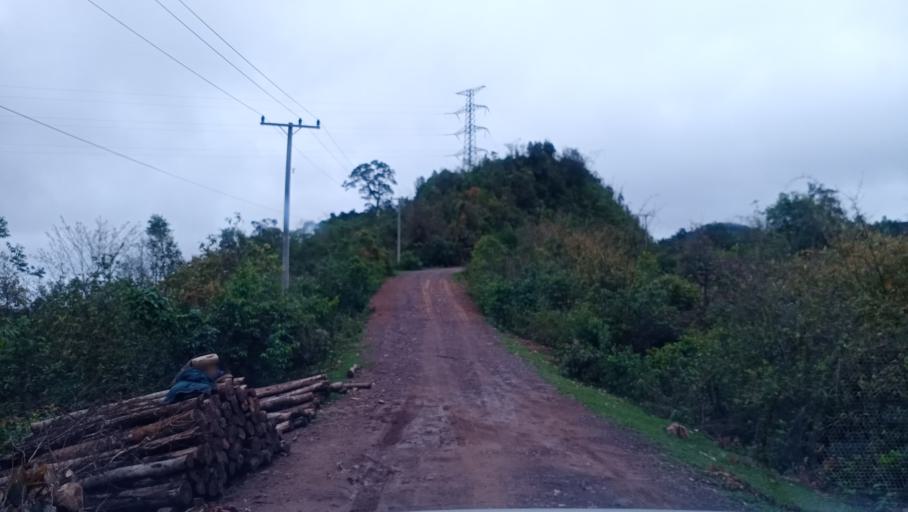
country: LA
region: Phongsali
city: Phongsali
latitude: 21.3409
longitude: 102.0850
